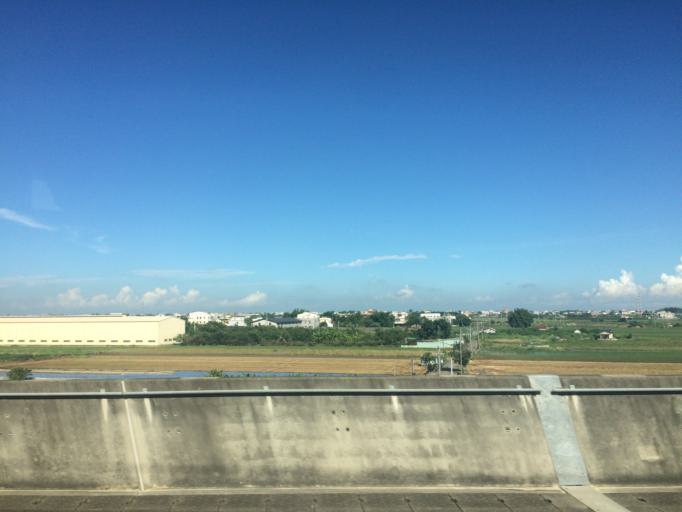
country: TW
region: Taiwan
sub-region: Chiayi
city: Taibao
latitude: 23.4987
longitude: 120.3258
